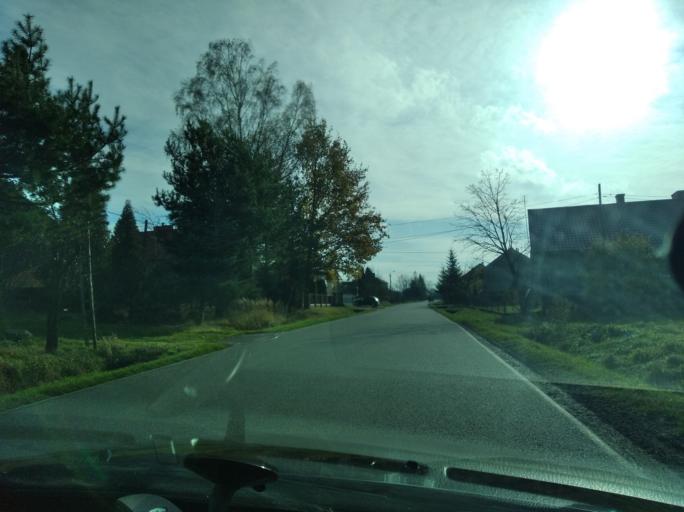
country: PL
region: Subcarpathian Voivodeship
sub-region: Powiat ropczycko-sedziszowski
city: Sedziszow Malopolski
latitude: 50.0836
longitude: 21.7502
